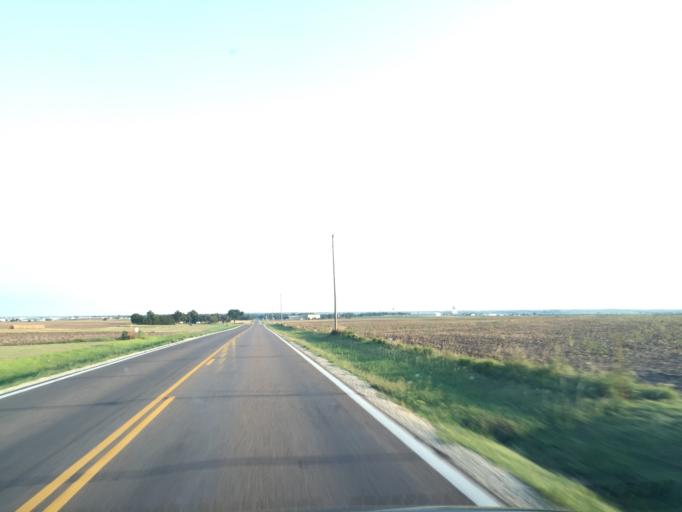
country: US
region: Kansas
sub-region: Ellsworth County
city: Ellsworth
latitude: 38.7612
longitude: -98.2251
